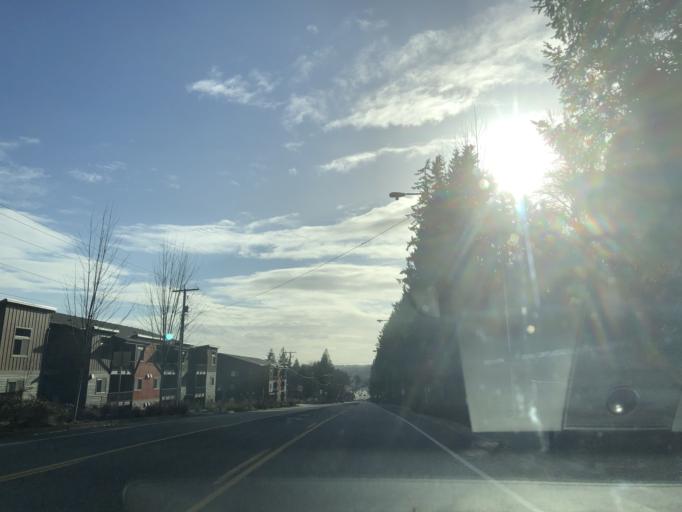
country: US
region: Washington
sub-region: Kitsap County
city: Poulsbo
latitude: 47.7557
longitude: -122.6529
